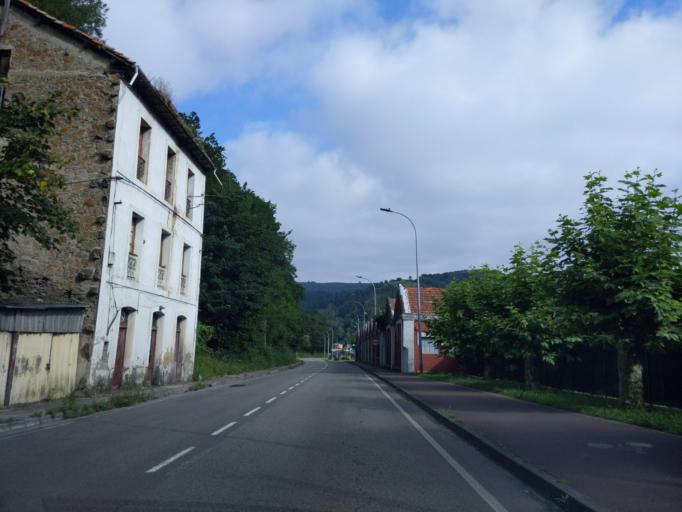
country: ES
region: Asturias
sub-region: Province of Asturias
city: El entrego
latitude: 43.2811
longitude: -5.6226
